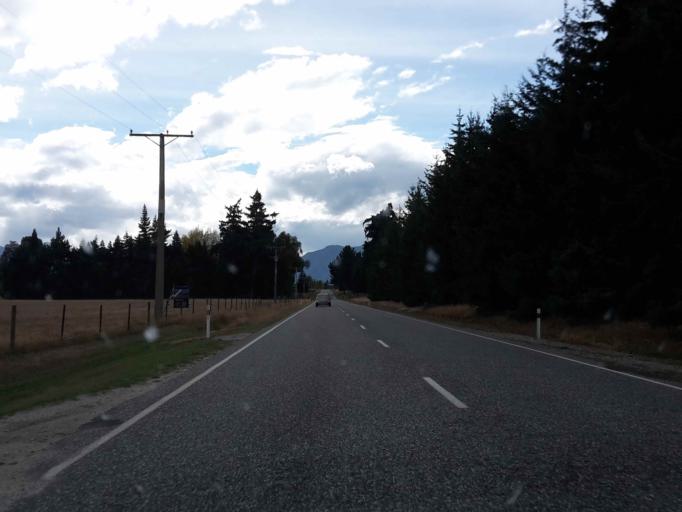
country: NZ
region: Otago
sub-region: Queenstown-Lakes District
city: Wanaka
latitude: -44.7237
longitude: 169.1369
